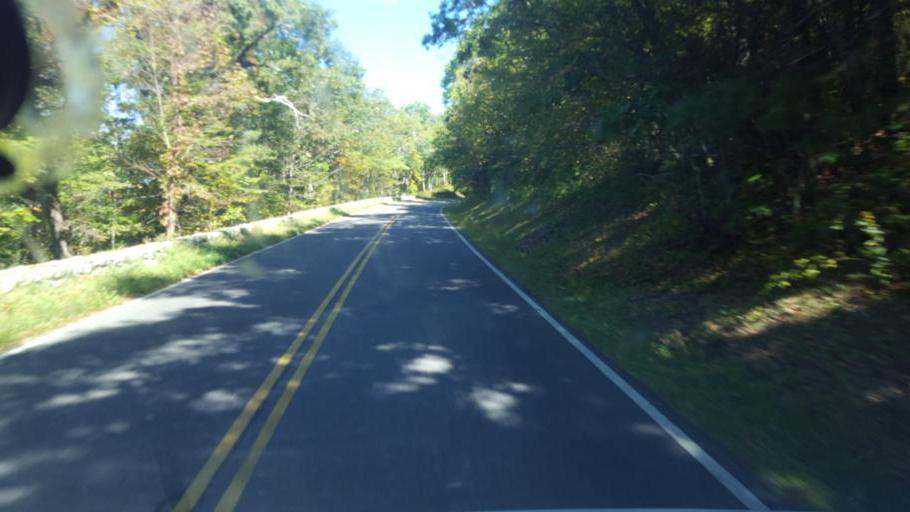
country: US
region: Virginia
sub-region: Greene County
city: Stanardsville
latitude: 38.4297
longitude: -78.4834
